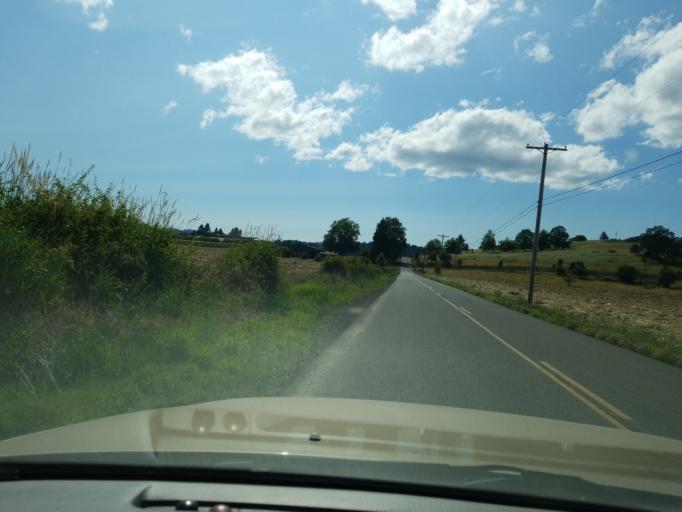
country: US
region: Oregon
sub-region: Yamhill County
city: McMinnville
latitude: 45.2451
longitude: -123.2164
